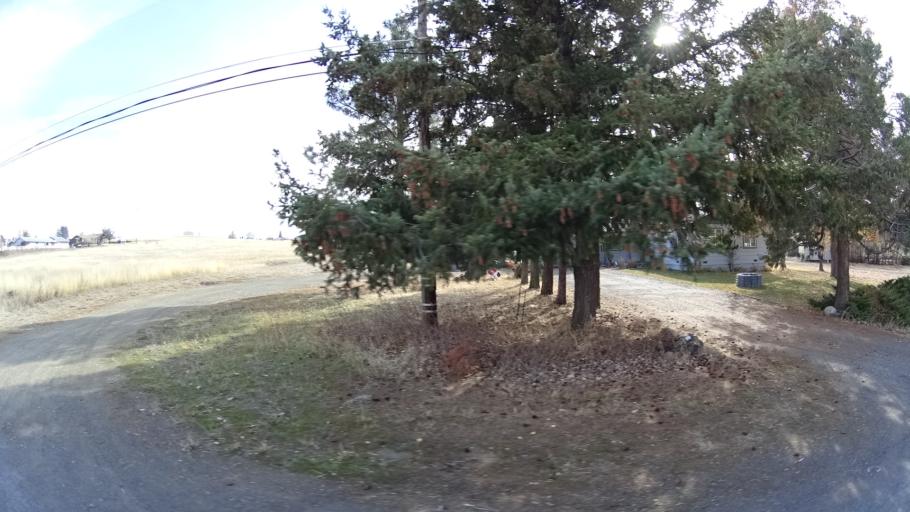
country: US
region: California
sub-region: Siskiyou County
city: Montague
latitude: 41.7307
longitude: -122.5220
